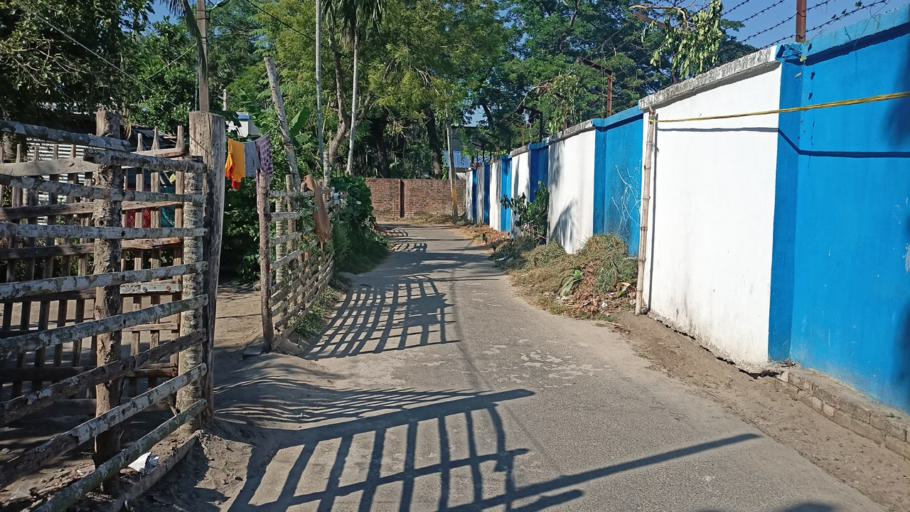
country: IN
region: West Bengal
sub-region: North 24 Parganas
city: Bangaon
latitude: 23.0528
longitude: 88.8253
